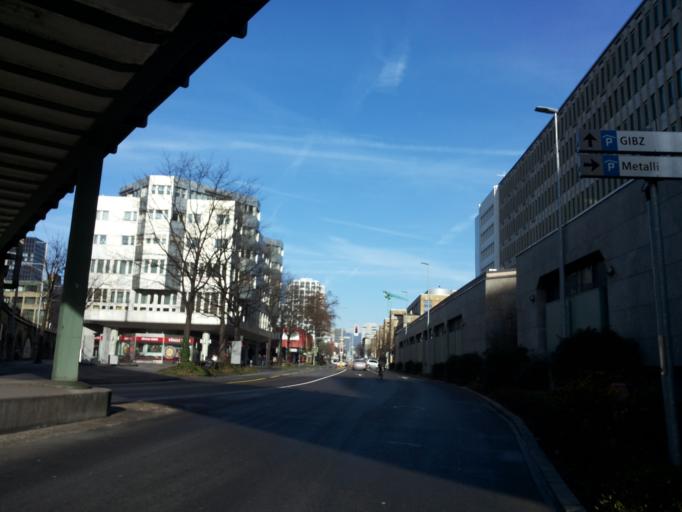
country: CH
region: Zug
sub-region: Zug
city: Zug
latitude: 47.1707
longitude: 8.5160
